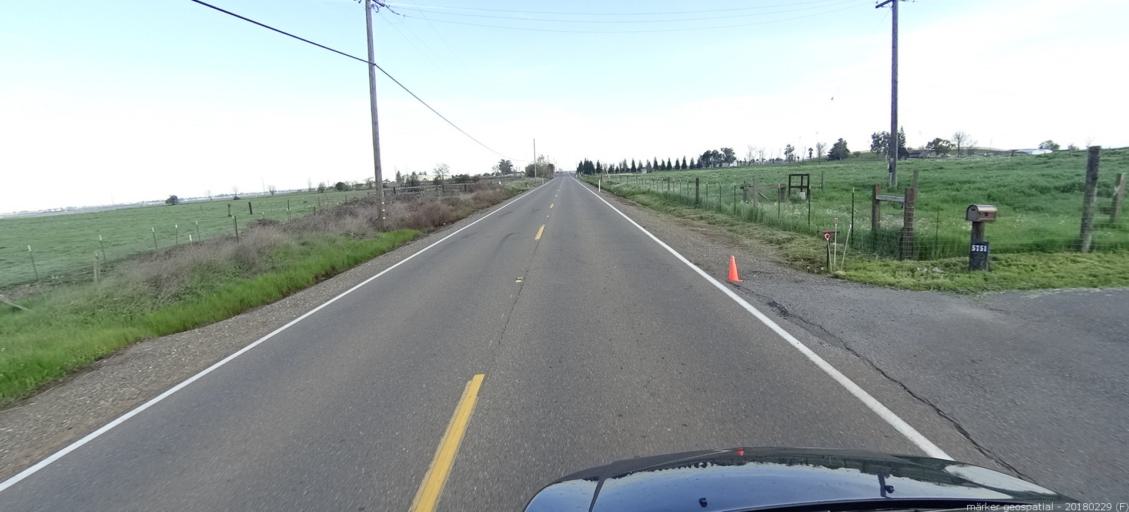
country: US
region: California
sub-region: Sacramento County
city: Rancho Cordova
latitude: 38.5230
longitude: -121.2979
